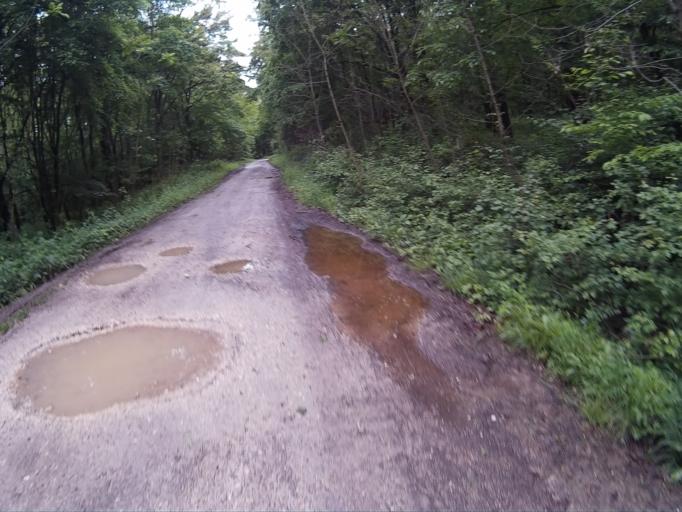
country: HU
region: Veszprem
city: Sumeg
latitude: 46.9045
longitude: 17.2685
